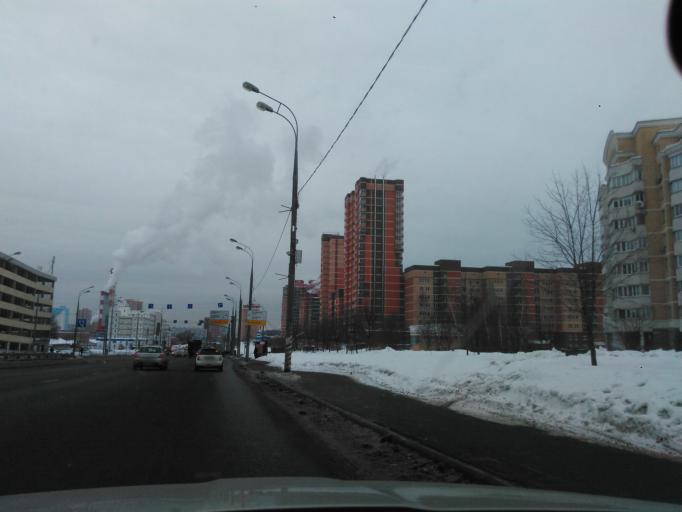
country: RU
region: Moscow
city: Khimki
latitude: 55.8999
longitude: 37.3984
